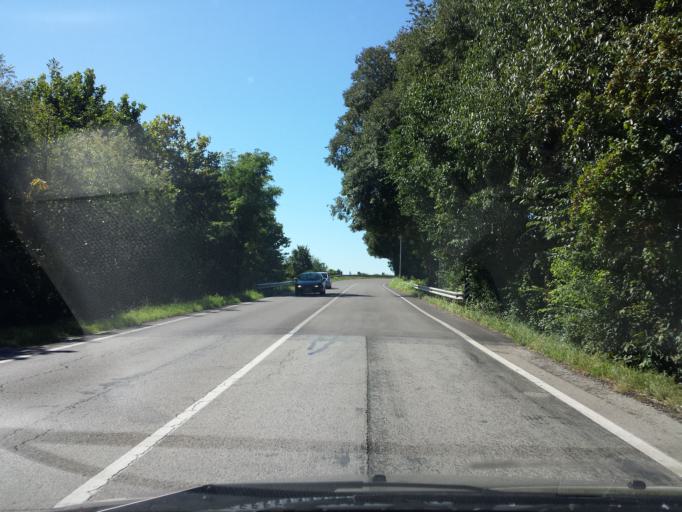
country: IT
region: Veneto
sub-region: Provincia di Vicenza
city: Dueville
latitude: 45.6178
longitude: 11.5674
